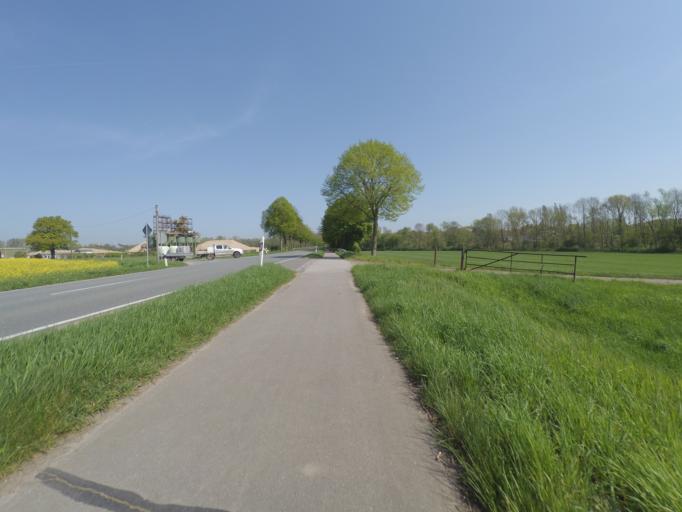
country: DE
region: North Rhine-Westphalia
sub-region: Regierungsbezirk Dusseldorf
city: Mehrhoog
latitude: 51.7144
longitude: 6.5101
